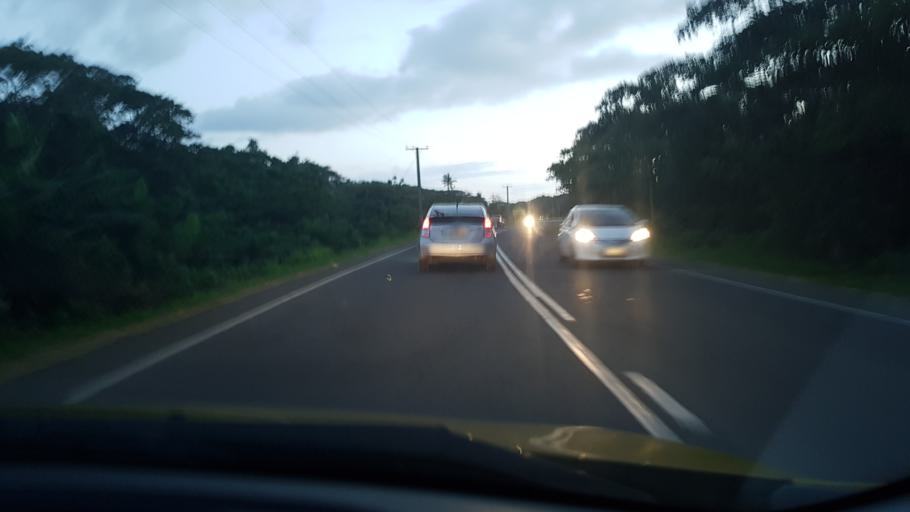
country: FJ
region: Western
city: Nadi
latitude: -18.1493
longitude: 177.5134
